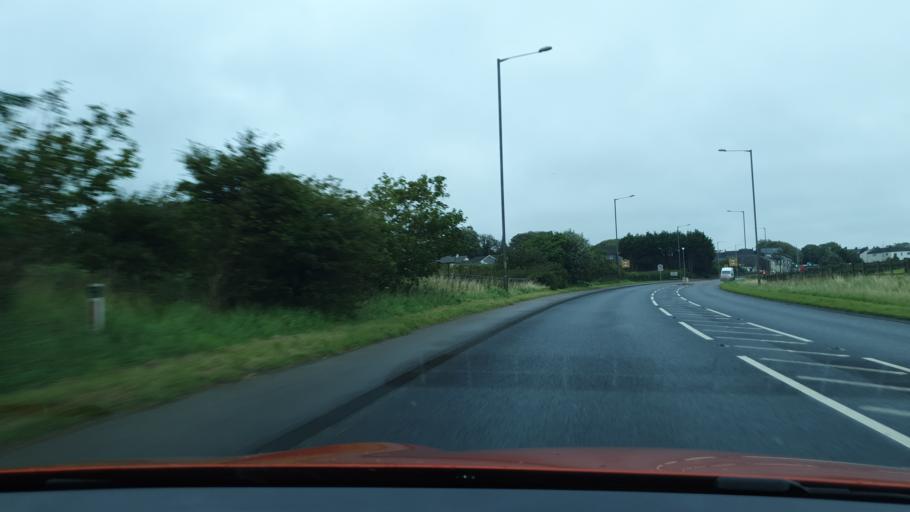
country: GB
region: England
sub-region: Cumbria
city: Dalton in Furness
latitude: 54.1710
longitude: -3.1550
